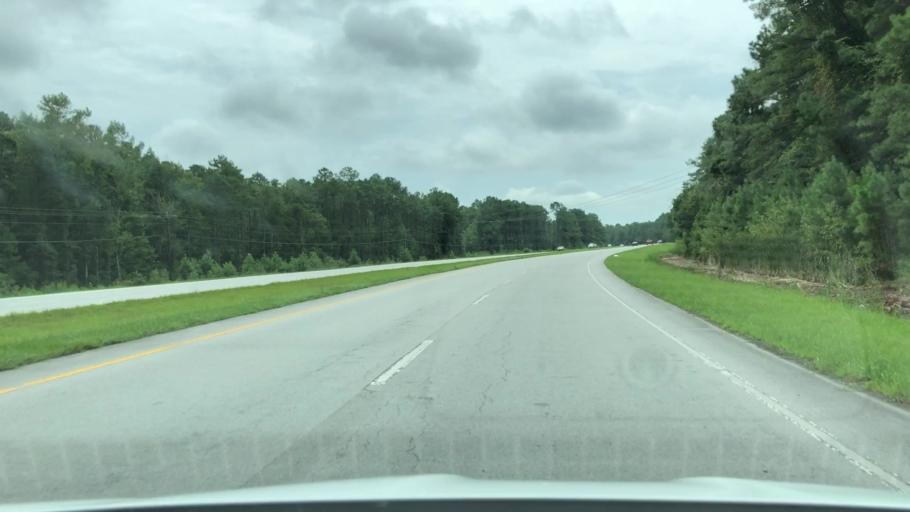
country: US
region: North Carolina
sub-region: Craven County
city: Havelock
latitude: 34.8427
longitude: -76.8825
